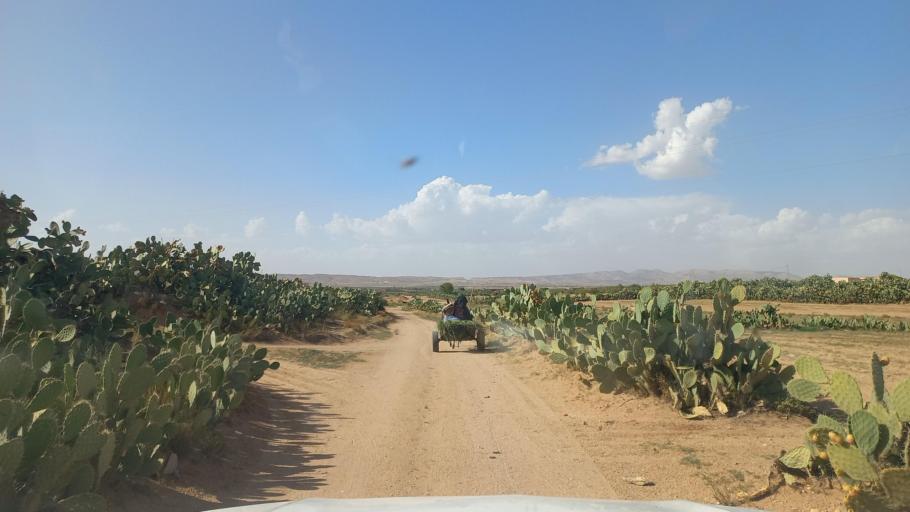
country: TN
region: Al Qasrayn
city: Sbiba
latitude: 35.3087
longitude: 9.0342
